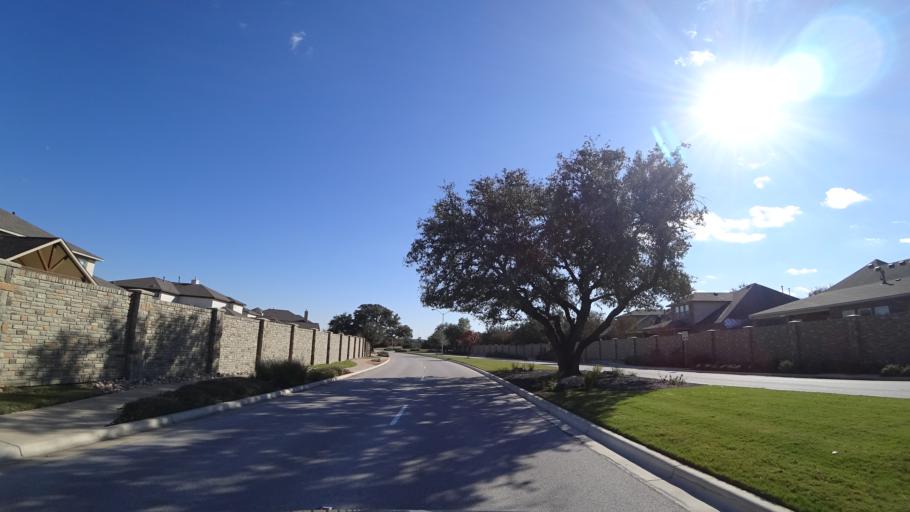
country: US
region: Texas
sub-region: Williamson County
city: Brushy Creek
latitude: 30.4893
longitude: -97.7218
